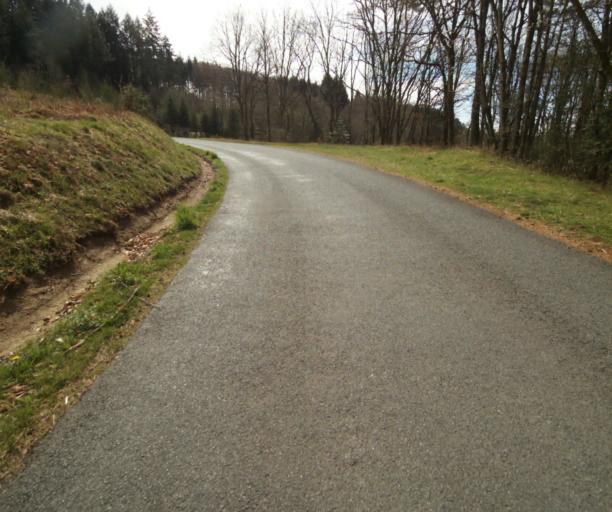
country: FR
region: Limousin
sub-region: Departement de la Correze
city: Correze
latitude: 45.3754
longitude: 1.9008
